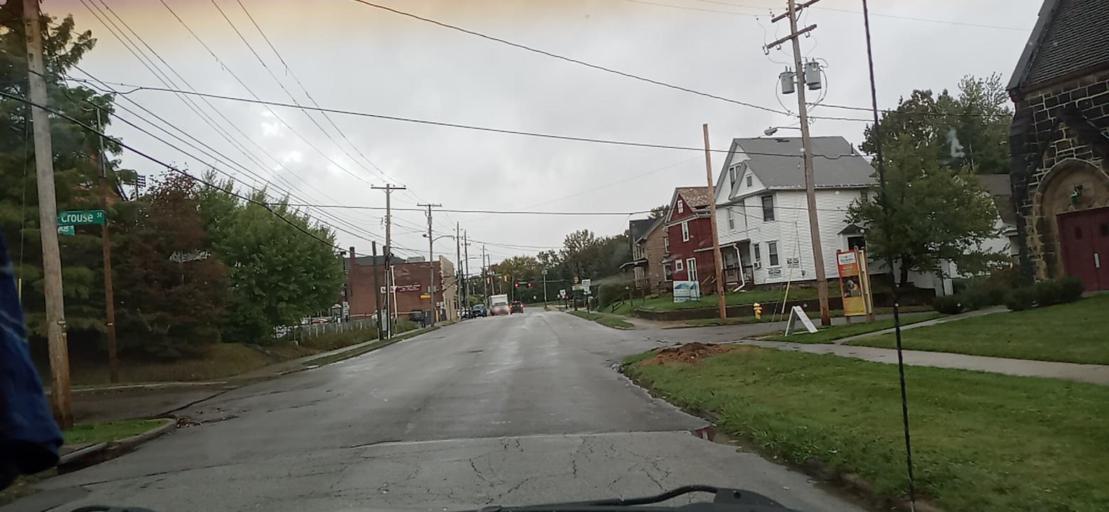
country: US
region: Ohio
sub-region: Summit County
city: Akron
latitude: 41.0698
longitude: -81.5073
